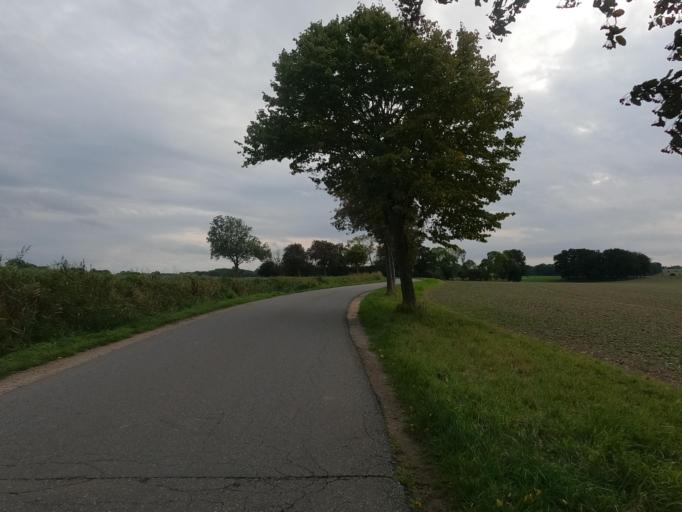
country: DE
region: Schleswig-Holstein
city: Heringsdorf
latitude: 54.2805
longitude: 11.0533
